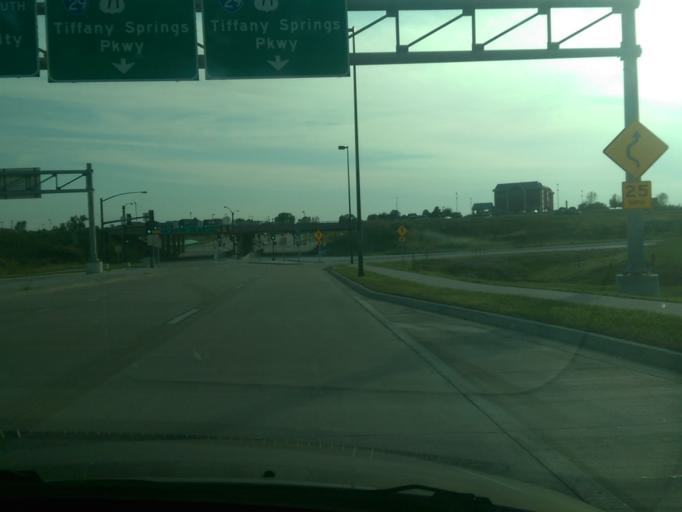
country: US
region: Missouri
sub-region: Platte County
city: Weatherby Lake
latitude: 39.2742
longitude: -94.6681
